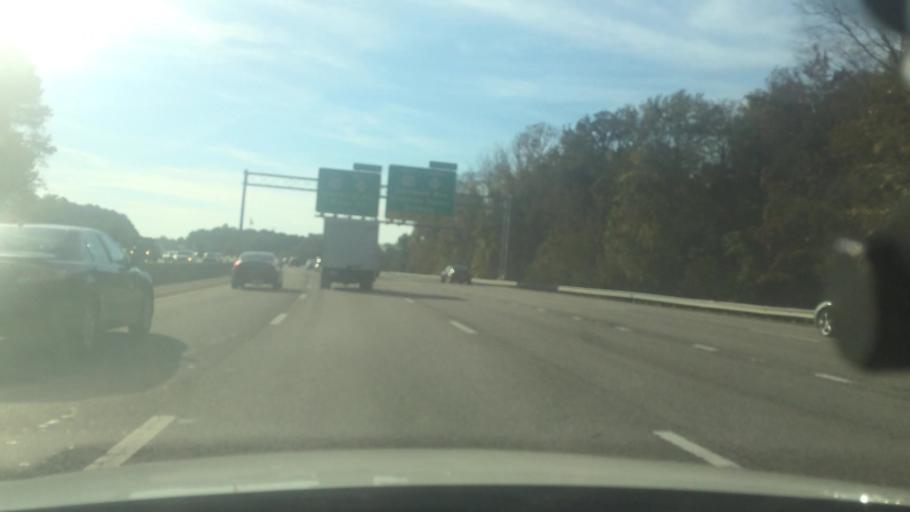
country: US
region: North Carolina
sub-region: Wake County
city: West Raleigh
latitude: 35.8369
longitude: -78.6647
